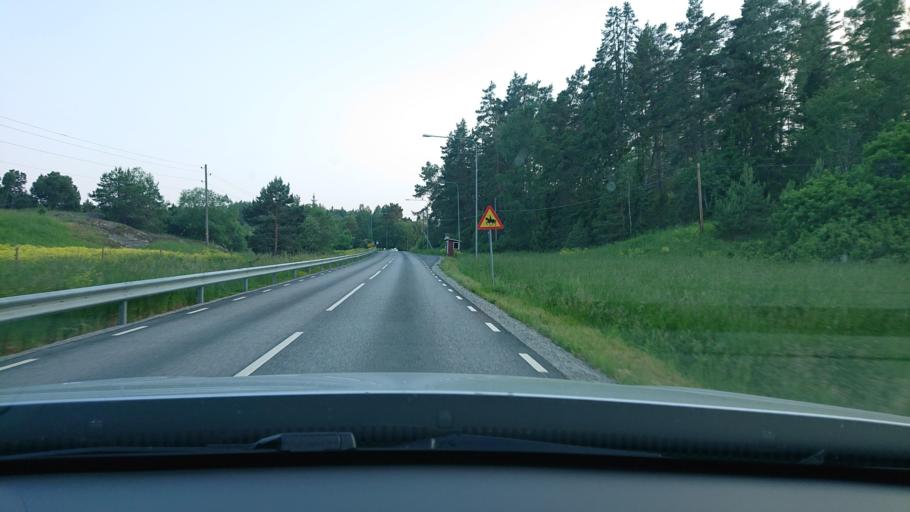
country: SE
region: Stockholm
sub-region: Vaxholms Kommun
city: Resaro
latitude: 59.4762
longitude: 18.3832
